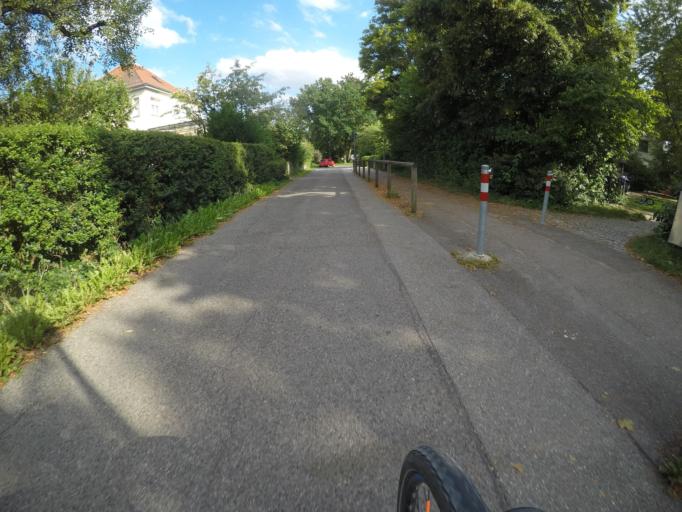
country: DE
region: Baden-Wuerttemberg
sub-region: Regierungsbezirk Stuttgart
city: Stuttgart-Ost
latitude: 48.7446
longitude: 9.2077
